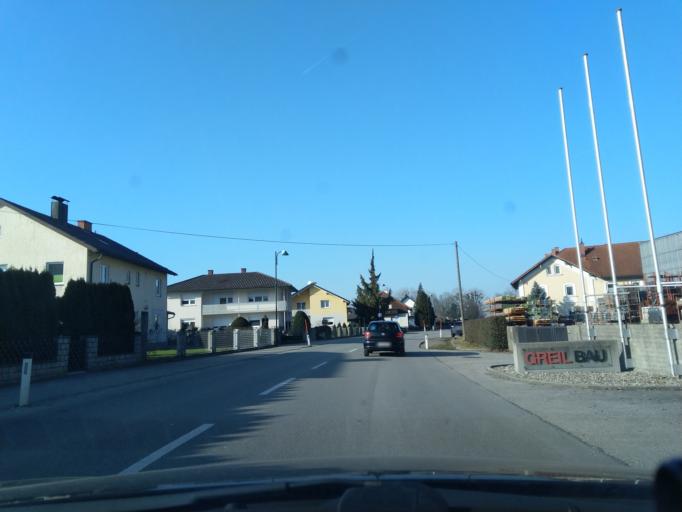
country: AT
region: Upper Austria
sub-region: Politischer Bezirk Scharding
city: Sankt Marienkirchen bei Schaerding
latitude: 48.2959
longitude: 13.4328
